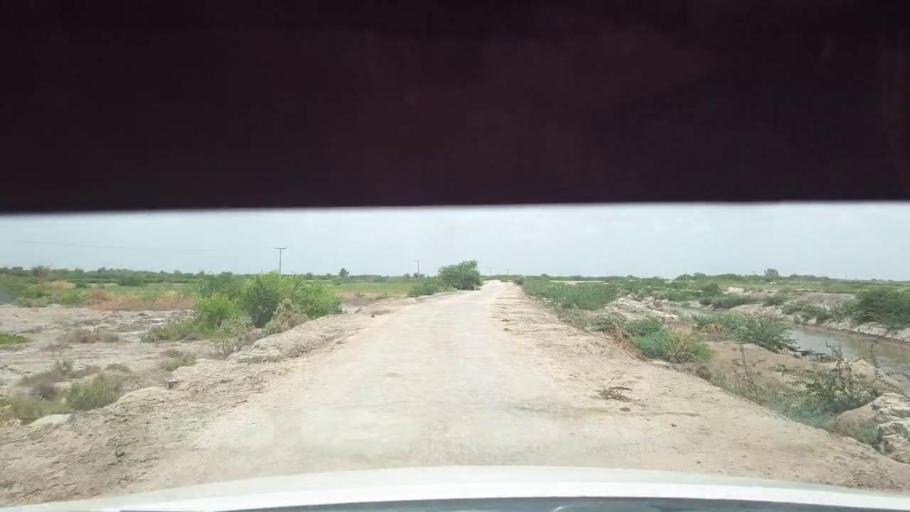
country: PK
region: Sindh
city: Kadhan
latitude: 24.4844
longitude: 69.0666
